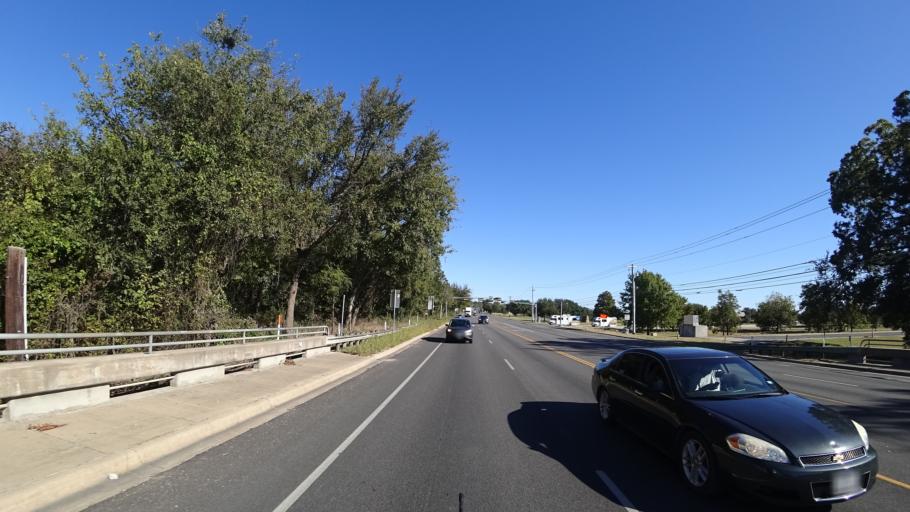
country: US
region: Texas
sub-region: Travis County
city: Hornsby Bend
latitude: 30.2832
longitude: -97.6541
